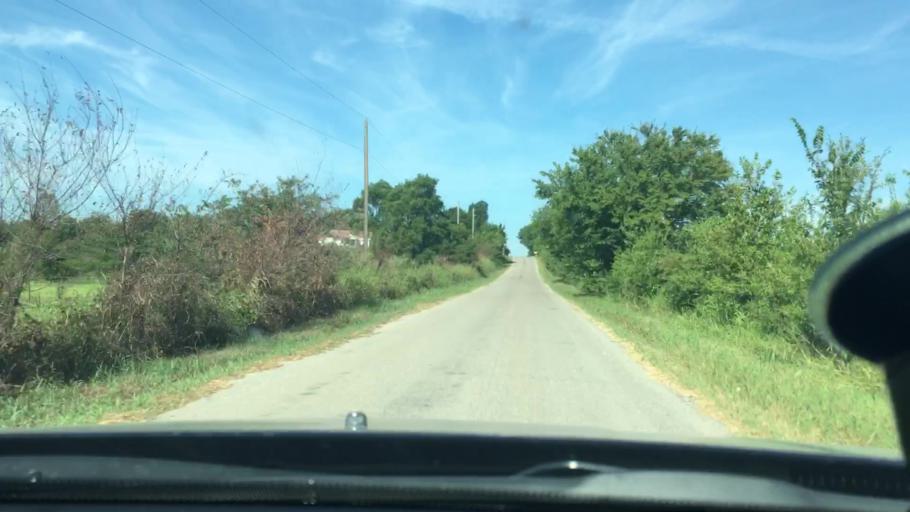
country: US
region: Oklahoma
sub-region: Carter County
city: Lone Grove
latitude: 34.2674
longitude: -97.2602
